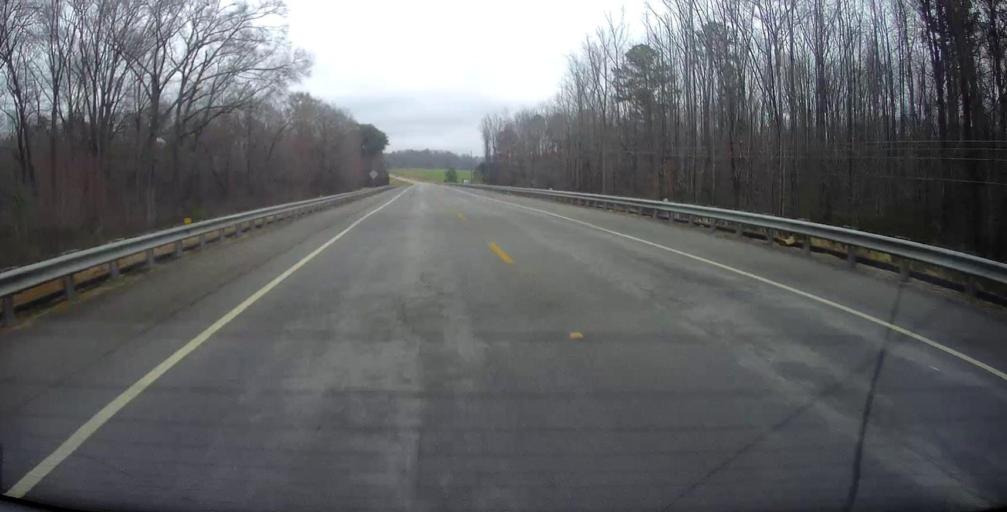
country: US
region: Georgia
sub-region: Lamar County
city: Barnesville
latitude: 33.0677
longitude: -84.2303
